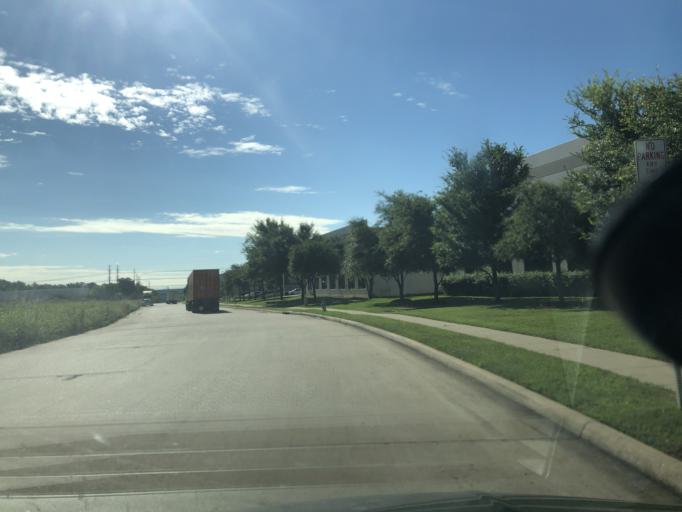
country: US
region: Texas
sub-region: Tarrant County
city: Euless
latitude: 32.8194
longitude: -97.0292
